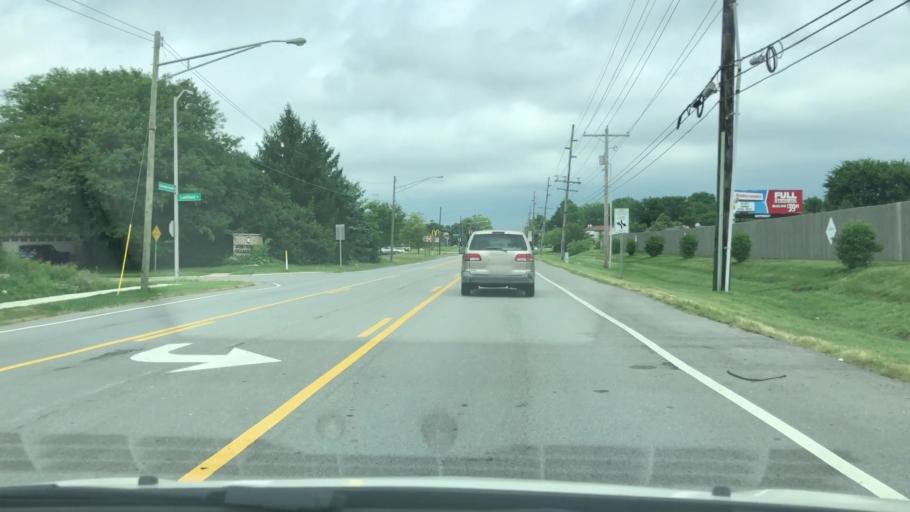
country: US
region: Ohio
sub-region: Franklin County
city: Worthington
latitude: 40.1168
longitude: -82.9897
